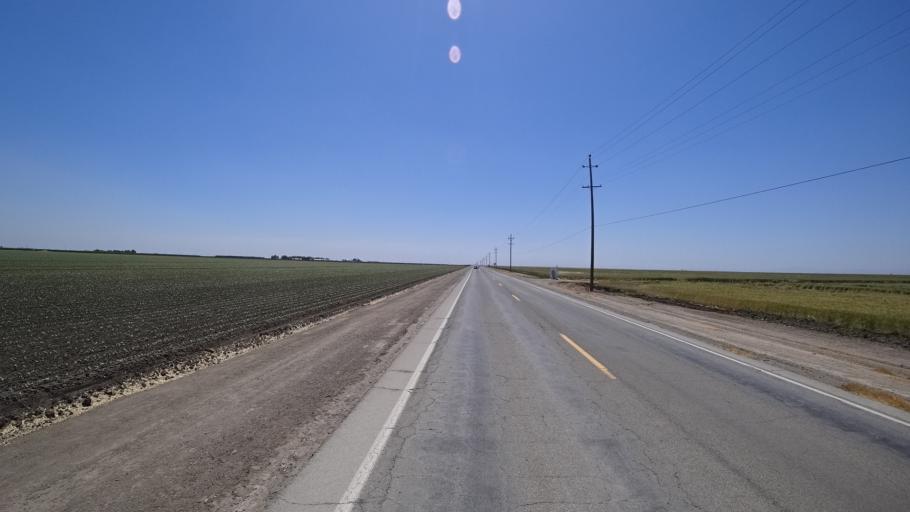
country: US
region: California
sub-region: Kings County
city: Corcoran
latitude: 36.1279
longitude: -119.6443
